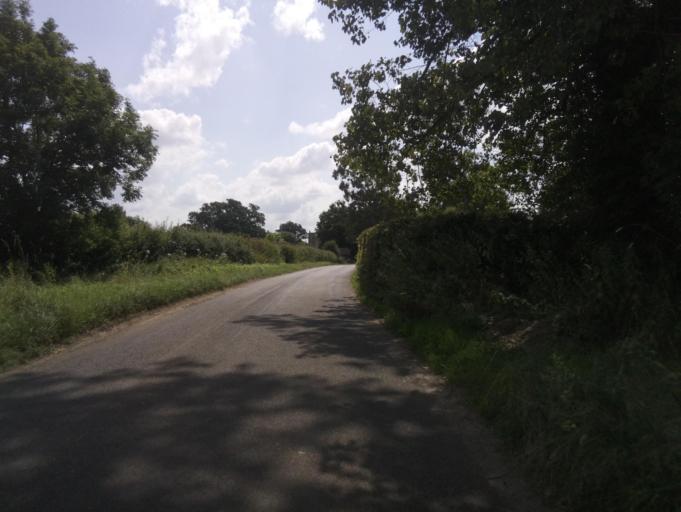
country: GB
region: England
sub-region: Wiltshire
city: Charlton
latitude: 51.6040
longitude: -2.0508
